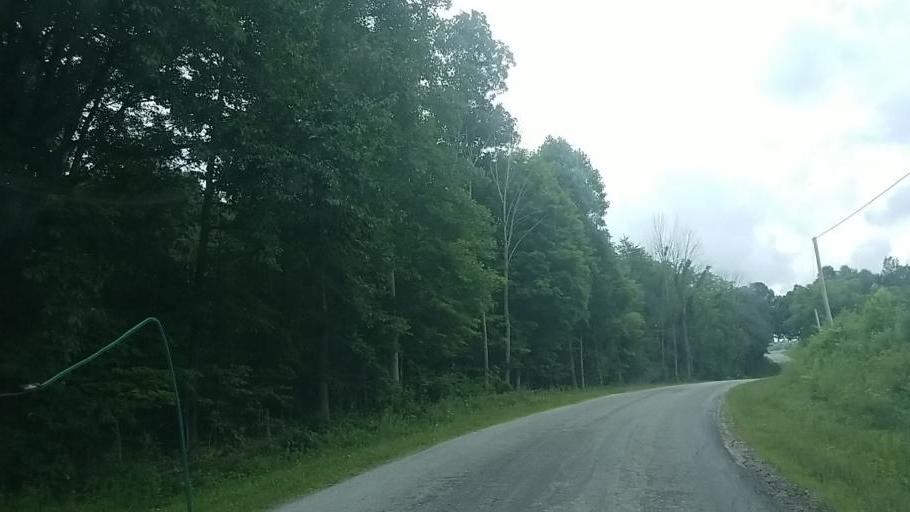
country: US
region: Ohio
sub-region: Muskingum County
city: Frazeysburg
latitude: 40.2158
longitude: -82.2541
